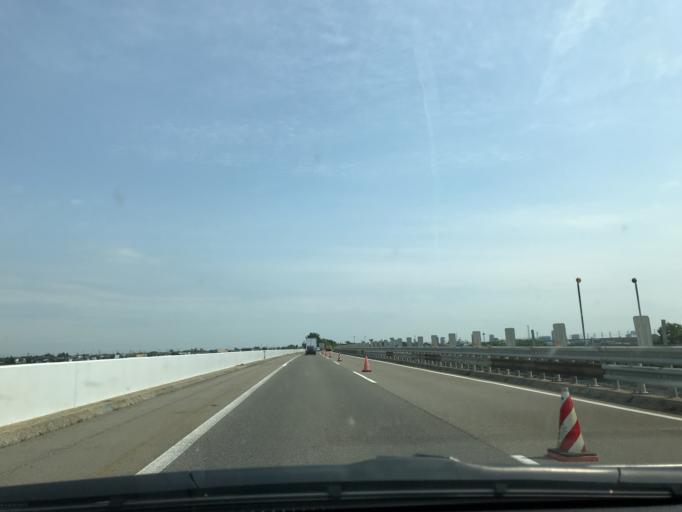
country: JP
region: Niigata
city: Sanjo
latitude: 37.6303
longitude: 138.9268
